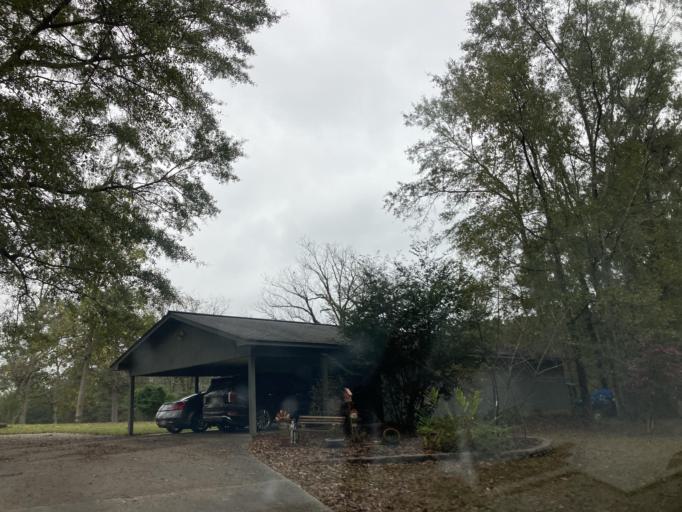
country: US
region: Mississippi
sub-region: Lamar County
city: Purvis
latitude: 31.1956
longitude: -89.4505
